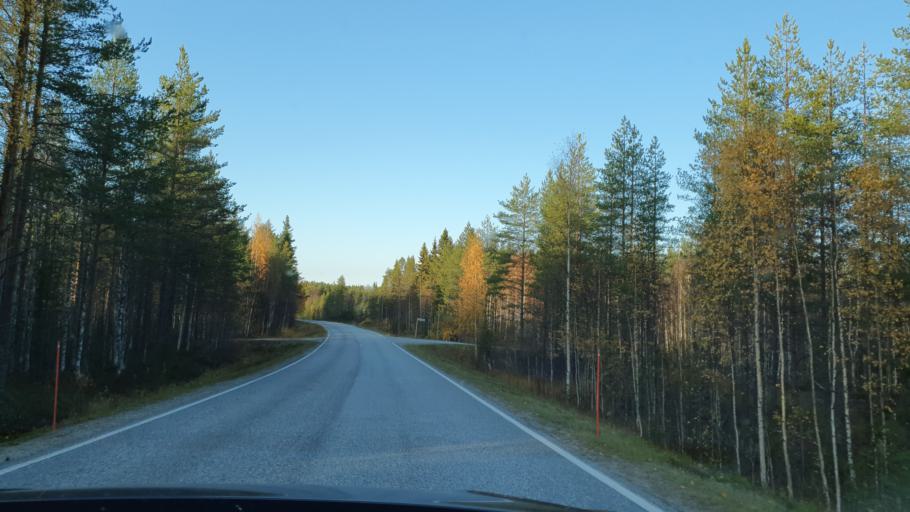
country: FI
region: Kainuu
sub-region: Kehys-Kainuu
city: Kuhmo
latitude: 64.3523
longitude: 29.4899
